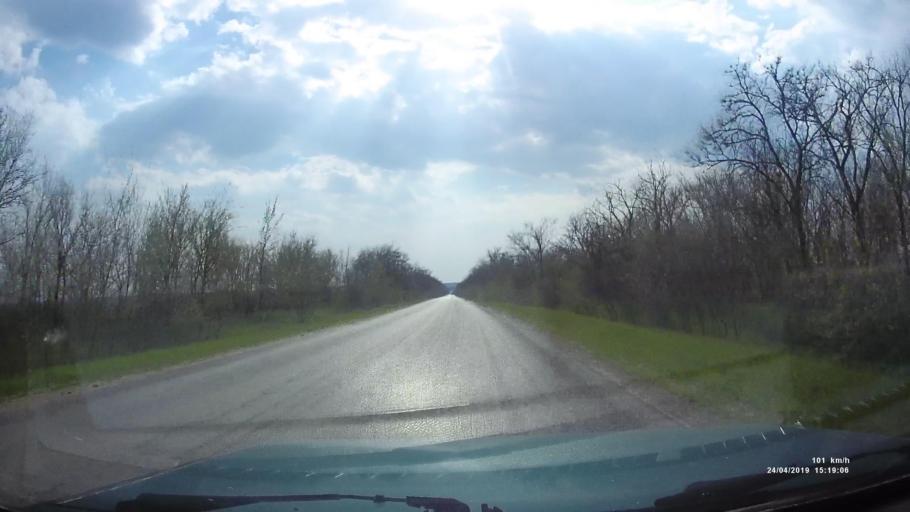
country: RU
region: Rostov
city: Remontnoye
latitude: 46.5424
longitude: 43.1530
